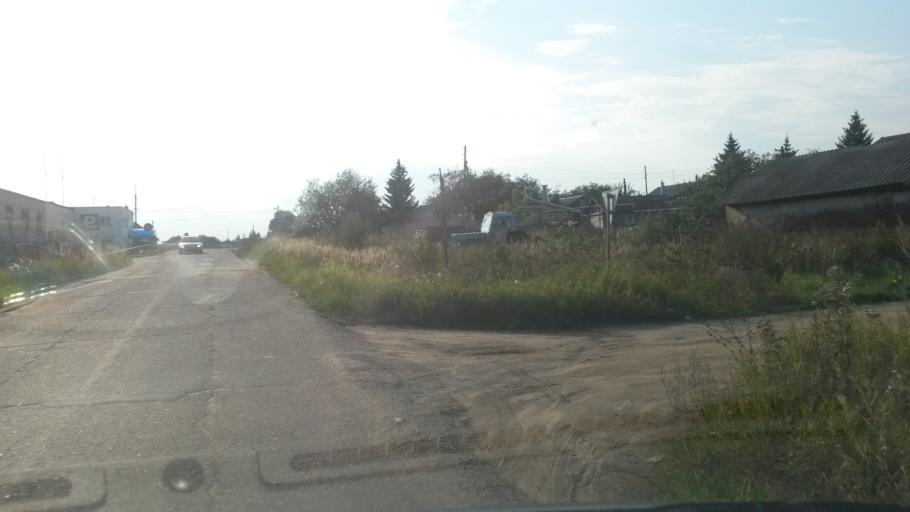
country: RU
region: Jaroslavl
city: Petrovsk
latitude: 56.9960
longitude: 39.2686
